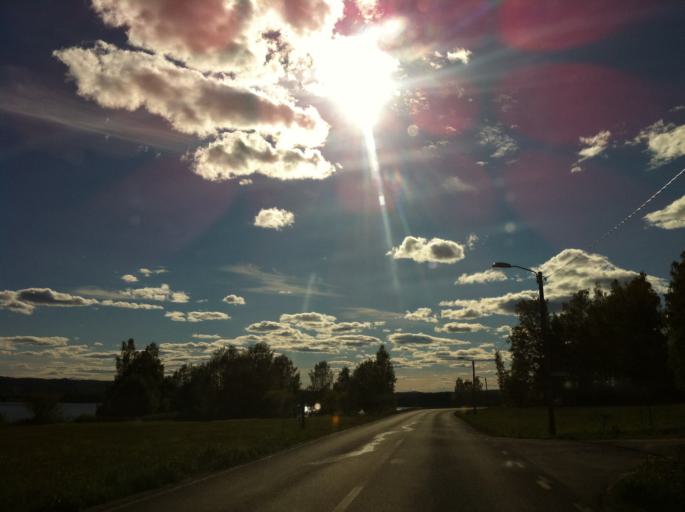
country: SE
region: Dalarna
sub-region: Leksand Municipality
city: Leksand
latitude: 60.7632
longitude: 14.9283
